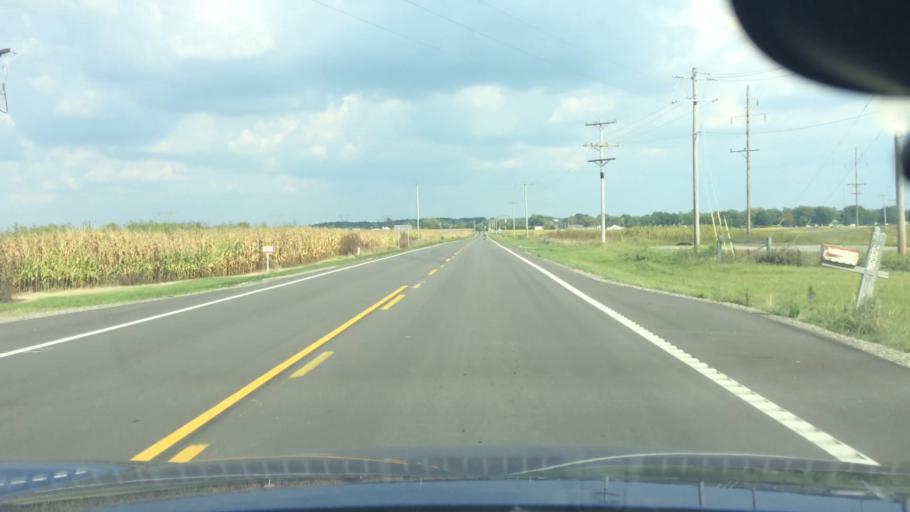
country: US
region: Ohio
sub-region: Logan County
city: Russells Point
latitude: 40.4459
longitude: -83.8195
